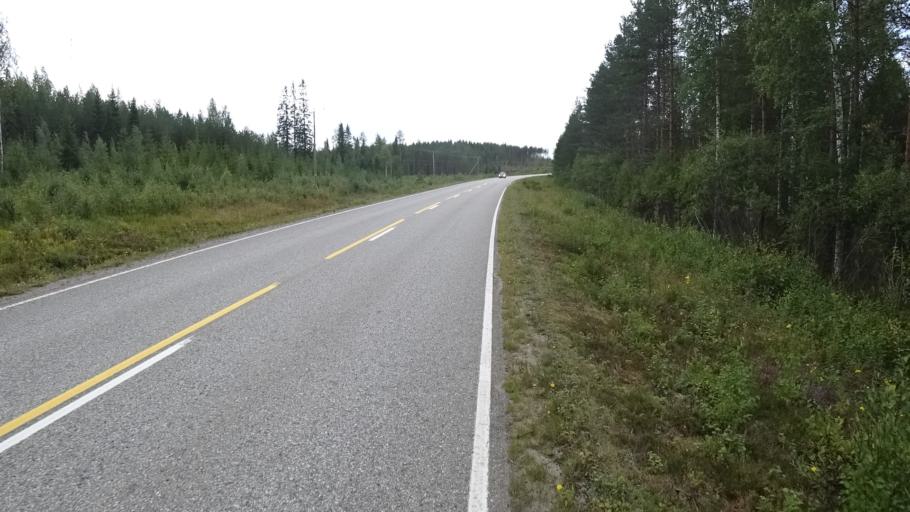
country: FI
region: North Karelia
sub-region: Joensuu
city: Ilomantsi
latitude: 62.6226
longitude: 31.2370
